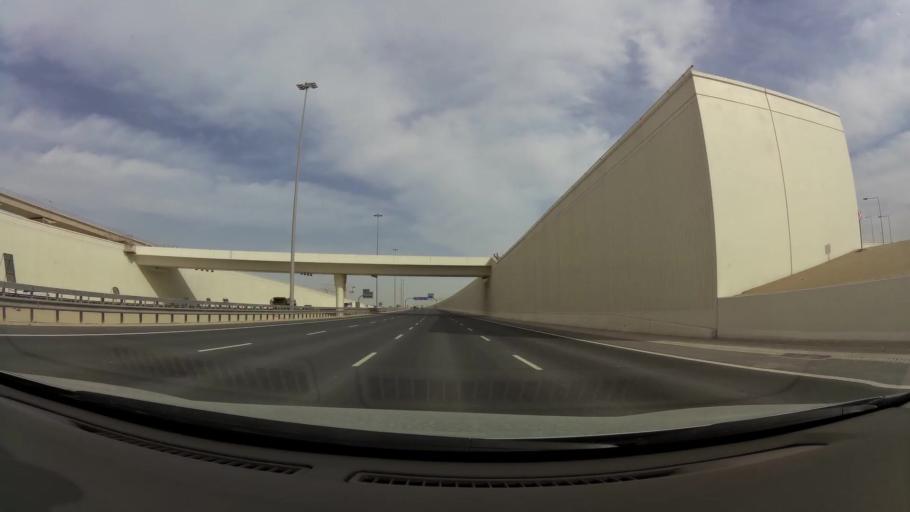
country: QA
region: Baladiyat ar Rayyan
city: Ar Rayyan
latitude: 25.3197
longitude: 51.3545
